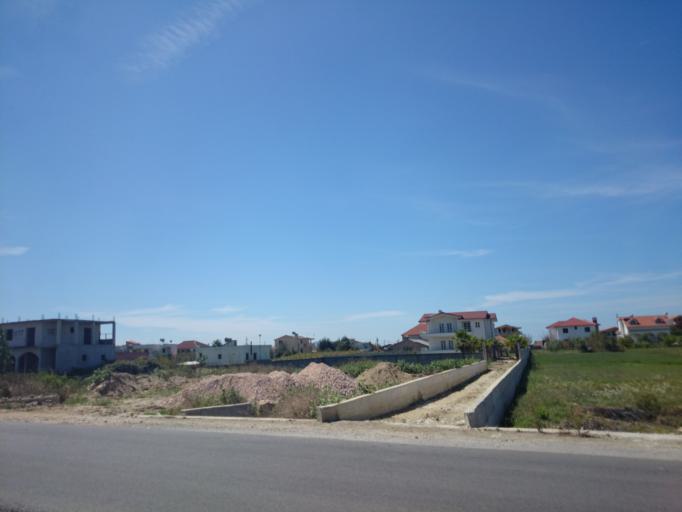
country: AL
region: Tirane
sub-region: Rrethi i Kavajes
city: Golem
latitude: 41.2193
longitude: 19.5293
